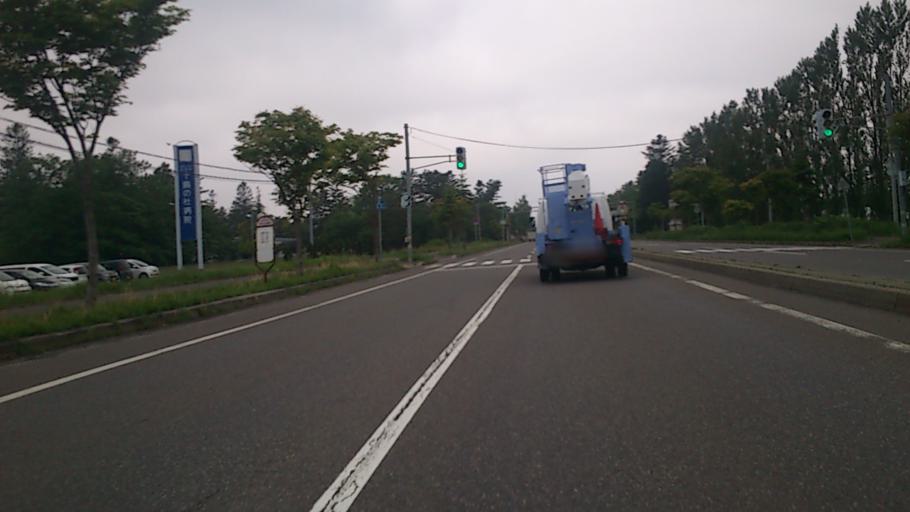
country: JP
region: Hokkaido
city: Obihiro
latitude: 42.9168
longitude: 143.2721
